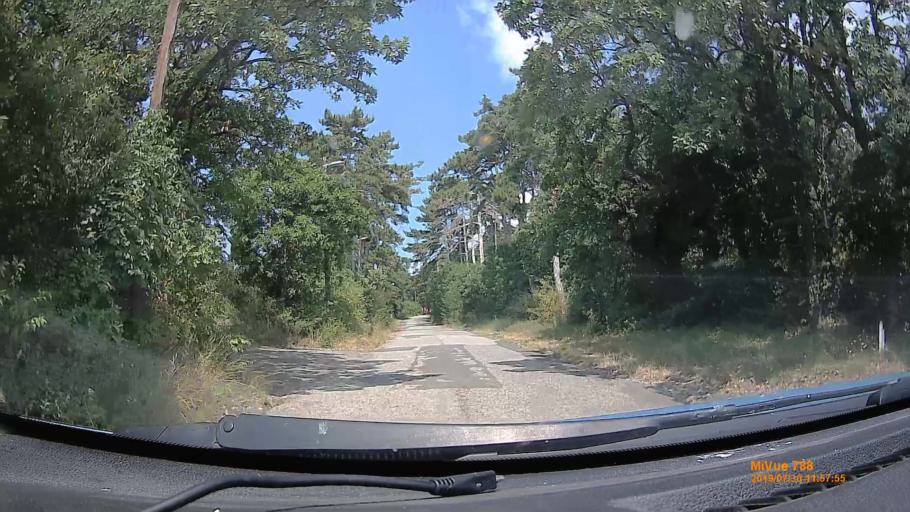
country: HU
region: Baranya
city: Pecs
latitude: 46.0898
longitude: 18.2156
